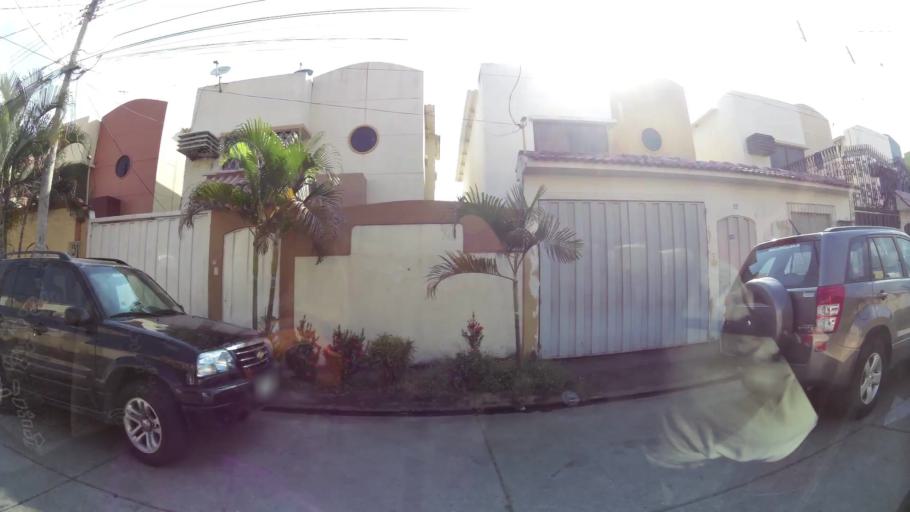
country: EC
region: Guayas
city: Guayaquil
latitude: -2.1370
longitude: -79.9271
